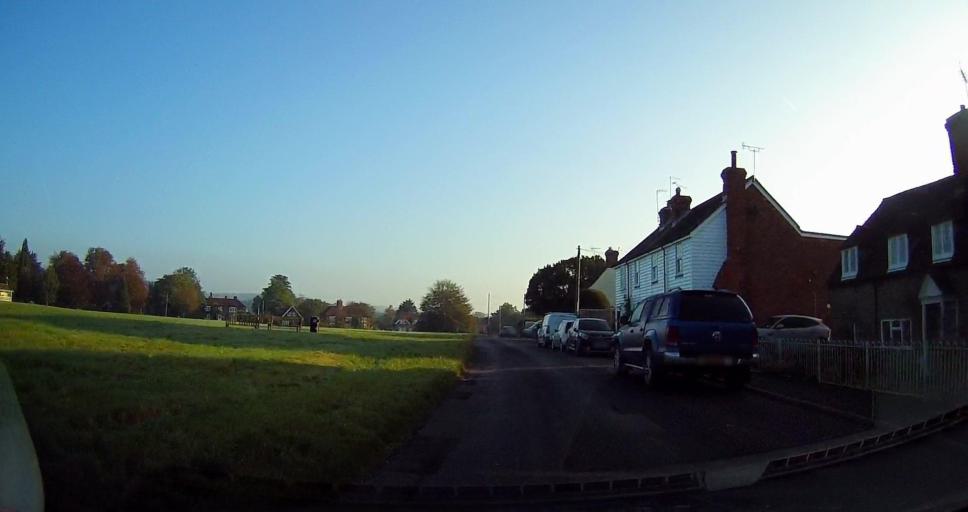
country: GB
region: England
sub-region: Kent
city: Kennington
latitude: 51.1878
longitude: 0.8919
